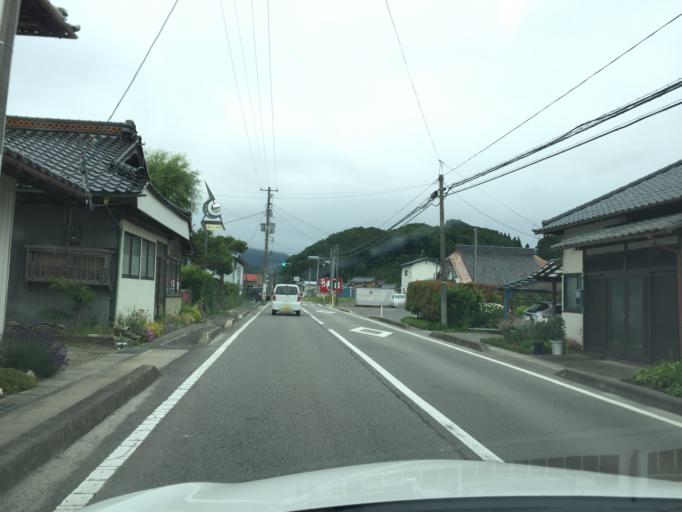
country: JP
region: Fukushima
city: Funehikimachi-funehiki
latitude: 37.3502
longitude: 140.6462
